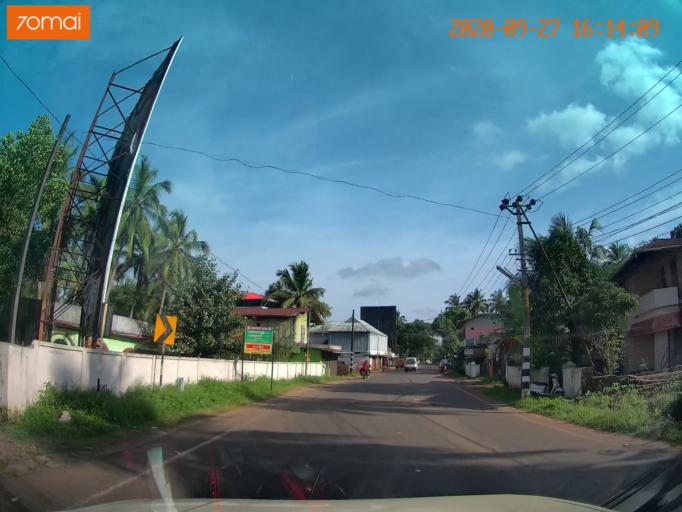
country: IN
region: Kerala
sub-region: Thrissur District
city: Trichur
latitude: 10.4649
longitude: 76.2470
